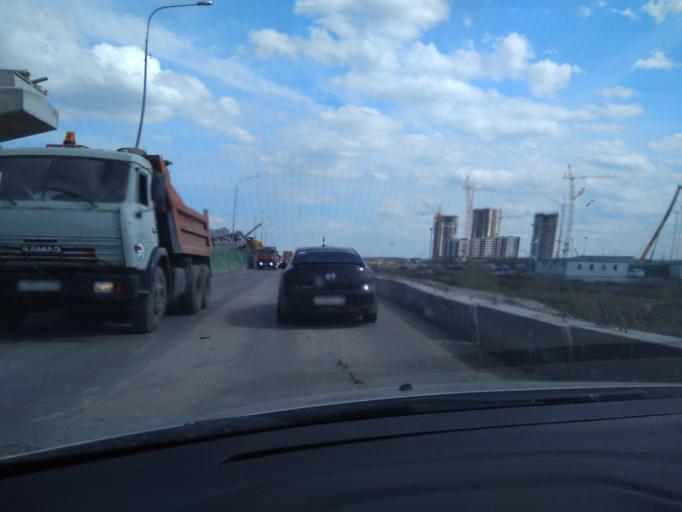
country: RU
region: Tjumen
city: Tyumen
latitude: 57.1042
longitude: 65.5631
